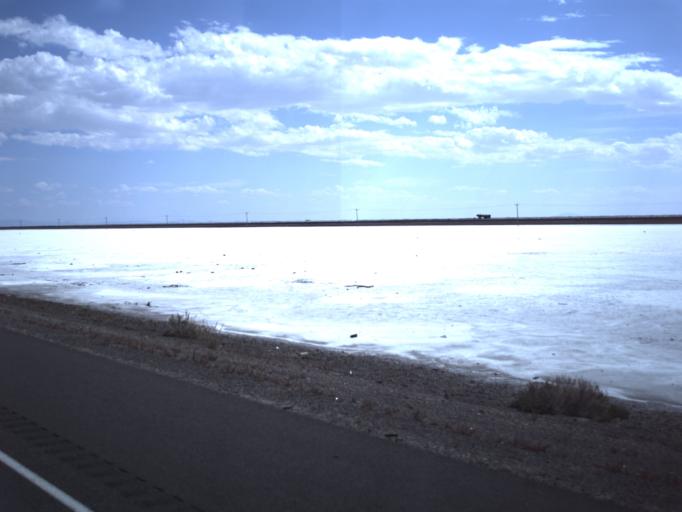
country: US
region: Utah
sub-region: Tooele County
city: Wendover
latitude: 40.7389
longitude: -113.8710
